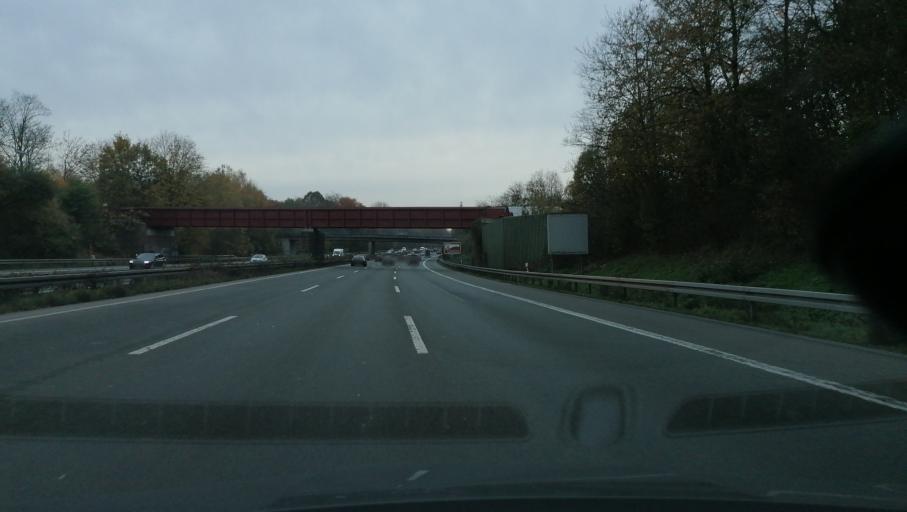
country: DE
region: North Rhine-Westphalia
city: Herten
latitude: 51.5772
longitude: 7.1632
